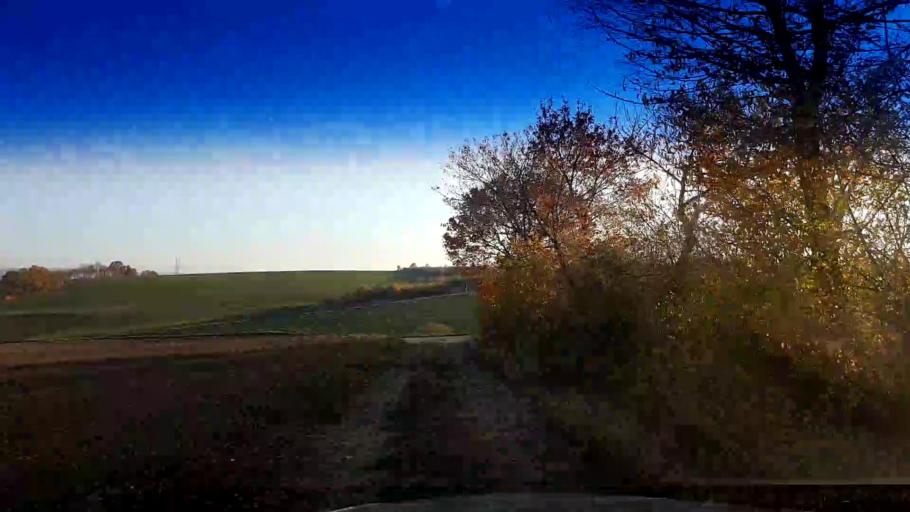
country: DE
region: Bavaria
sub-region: Upper Franconia
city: Memmelsdorf
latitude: 49.9710
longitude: 10.9721
